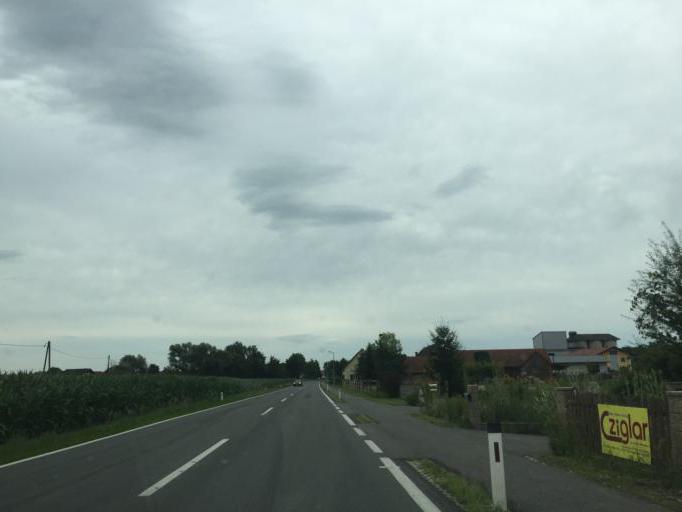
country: AT
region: Styria
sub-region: Politischer Bezirk Suedoststeiermark
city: Ratschendorf
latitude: 46.7283
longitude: 15.8274
